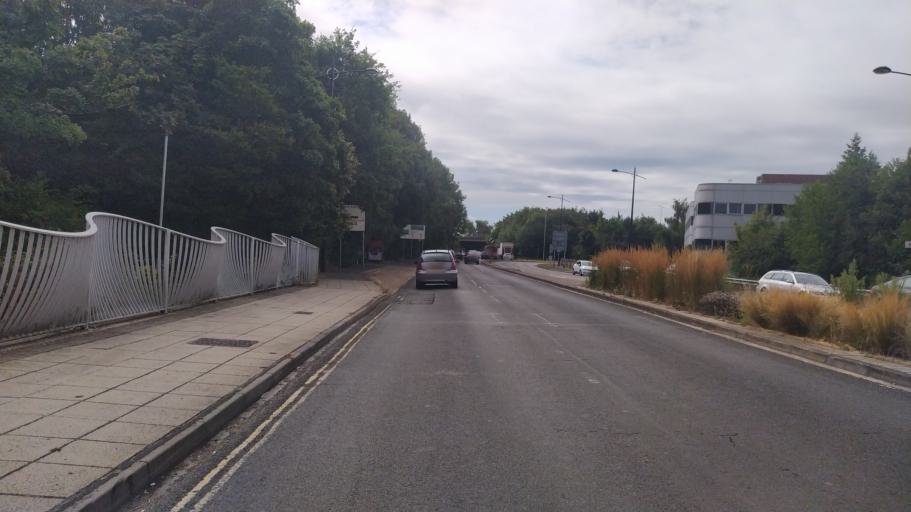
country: GB
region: England
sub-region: Hampshire
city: Havant
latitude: 50.8499
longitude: -0.9843
